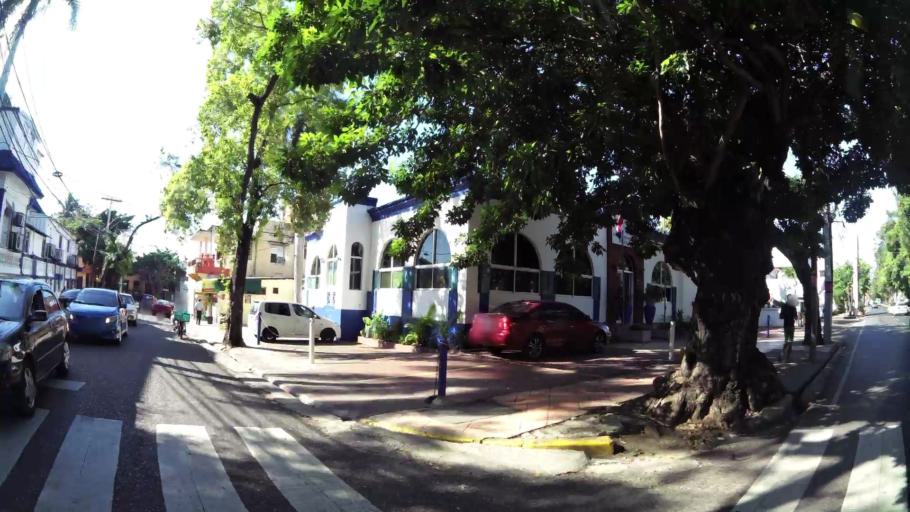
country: DO
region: Nacional
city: Ciudad Nueva
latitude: 18.4710
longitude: -69.8952
